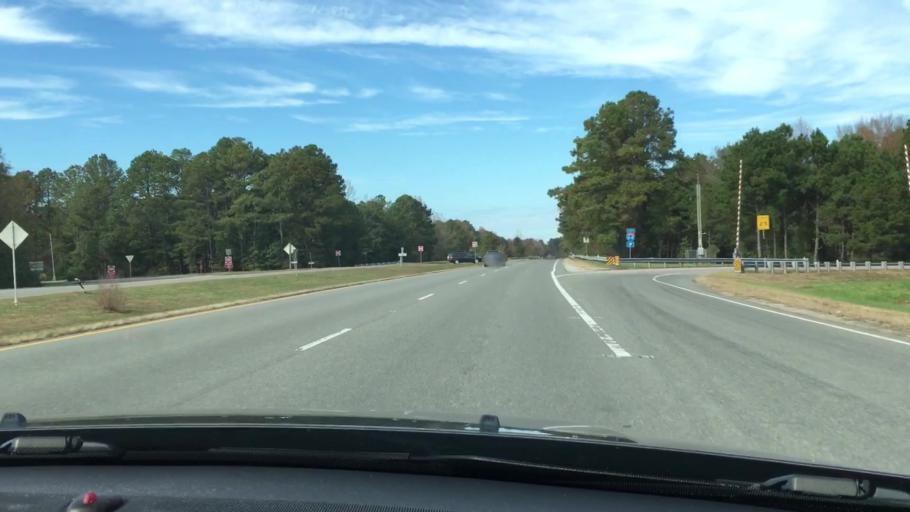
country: US
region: Virginia
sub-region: King William County
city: West Point
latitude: 37.4186
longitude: -76.8220
